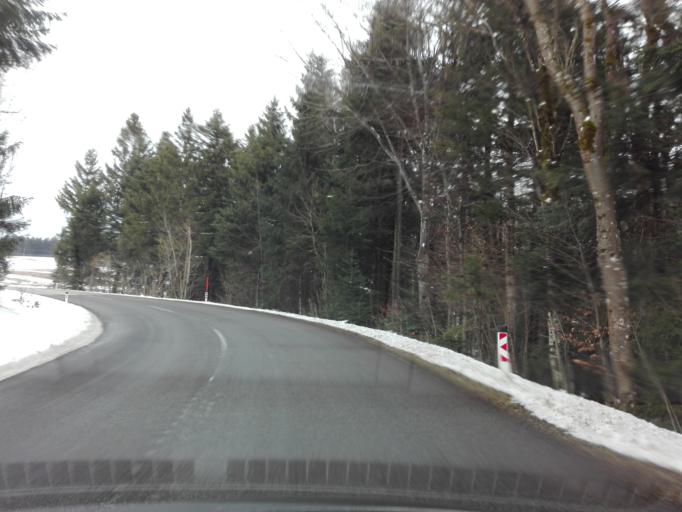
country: DE
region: Bavaria
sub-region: Lower Bavaria
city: Wegscheid
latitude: 48.5543
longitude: 13.8068
